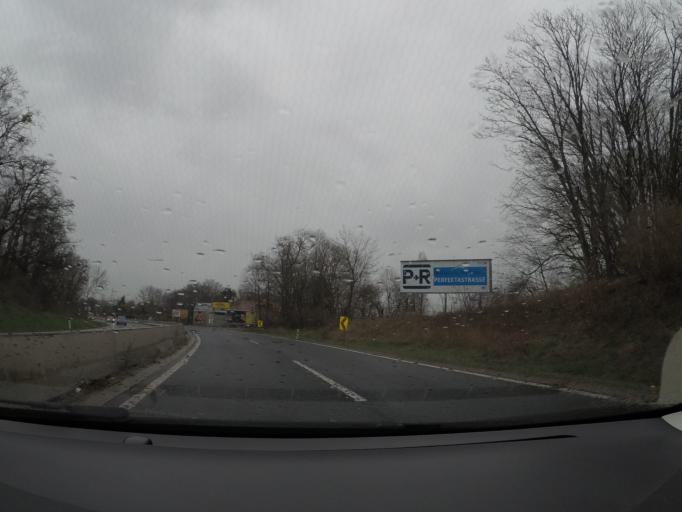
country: AT
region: Lower Austria
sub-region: Politischer Bezirk Modling
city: Brunn am Gebirge
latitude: 48.1254
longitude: 16.2984
